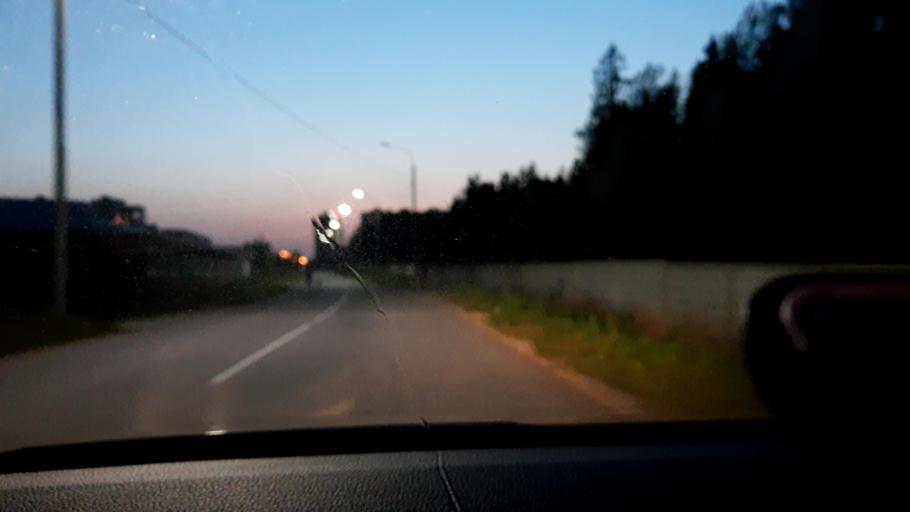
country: RU
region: Moskovskaya
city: Krasnoznamensk
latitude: 55.5838
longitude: 37.0496
